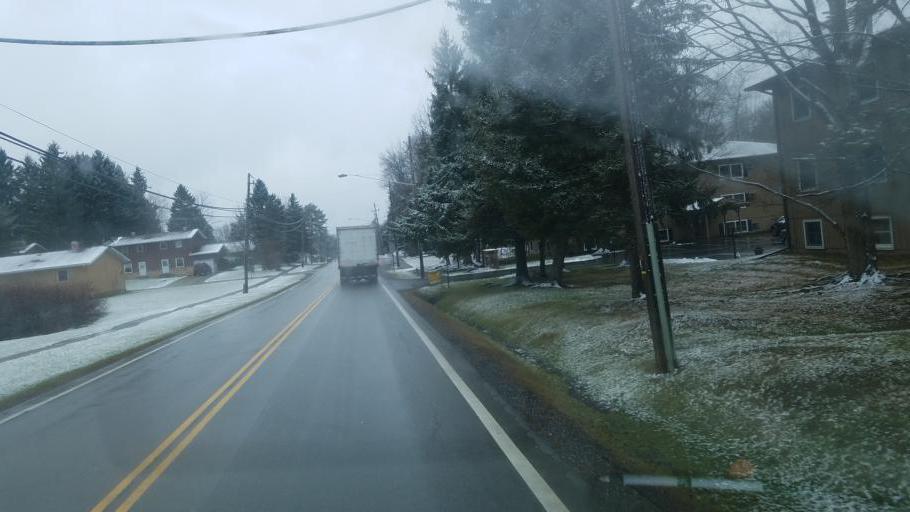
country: US
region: Ohio
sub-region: Portage County
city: Garrettsville
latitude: 41.2739
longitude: -81.0985
